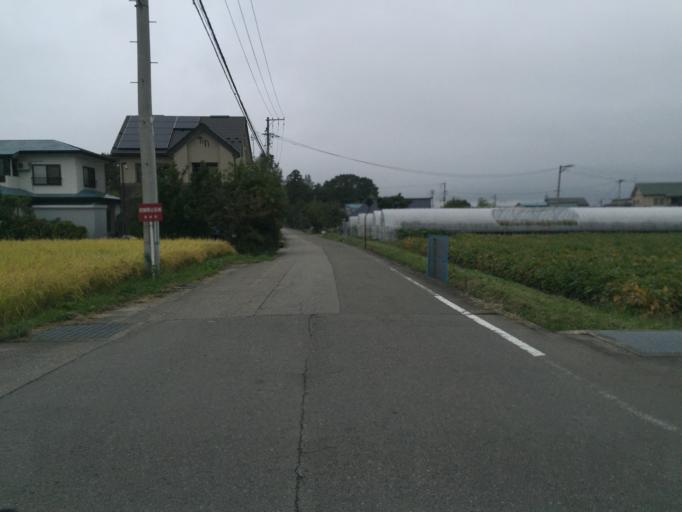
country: JP
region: Fukushima
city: Kitakata
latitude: 37.4535
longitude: 139.9155
